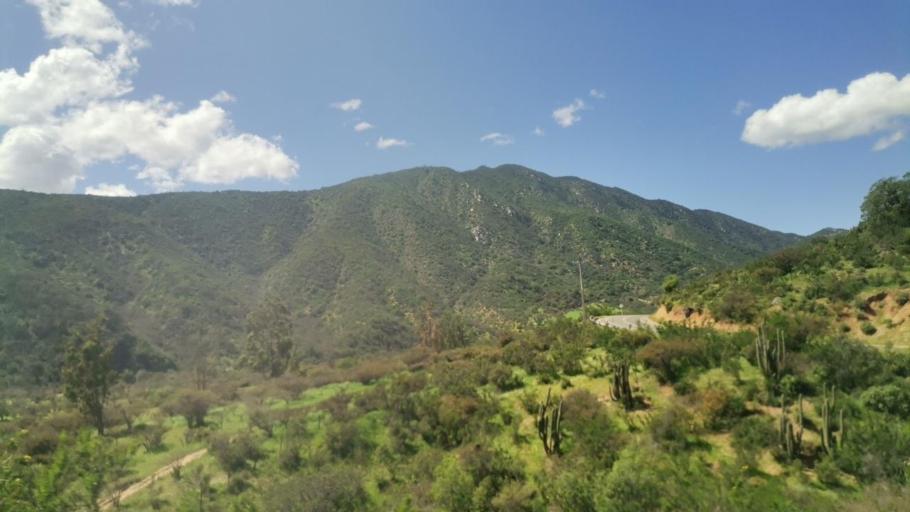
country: CL
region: Valparaiso
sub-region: Provincia de Marga Marga
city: Villa Alemana
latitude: -33.1901
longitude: -71.2894
